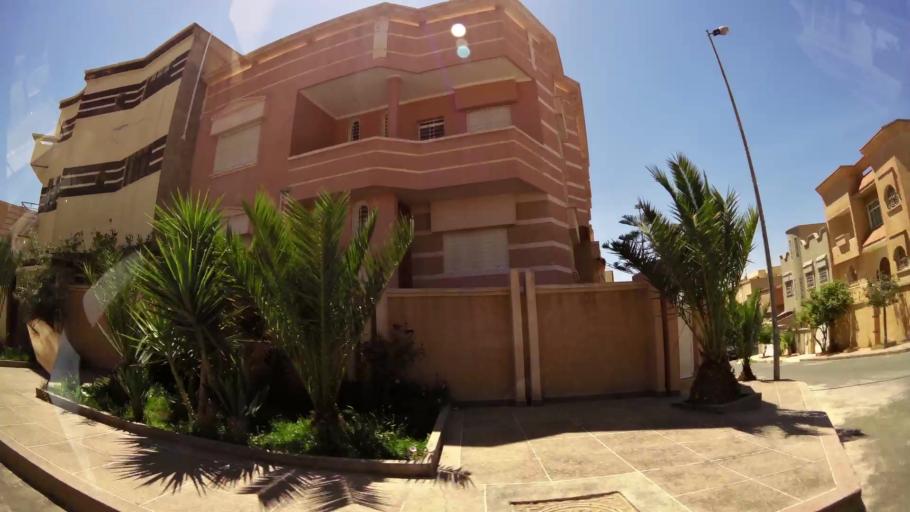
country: MA
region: Oriental
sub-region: Oujda-Angad
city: Oujda
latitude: 34.6524
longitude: -1.9156
